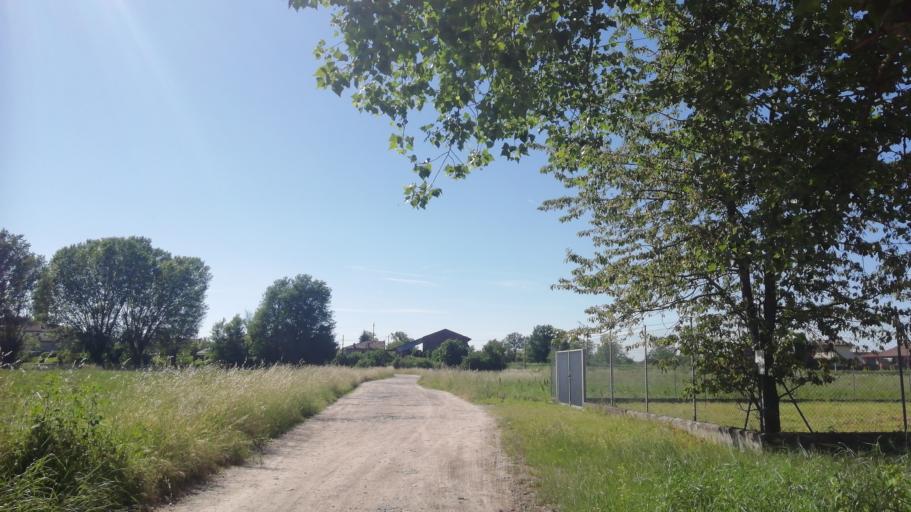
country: IT
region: Emilia-Romagna
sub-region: Provincia di Piacenza
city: Borgonovo Valtidone
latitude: 44.9906
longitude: 9.4757
